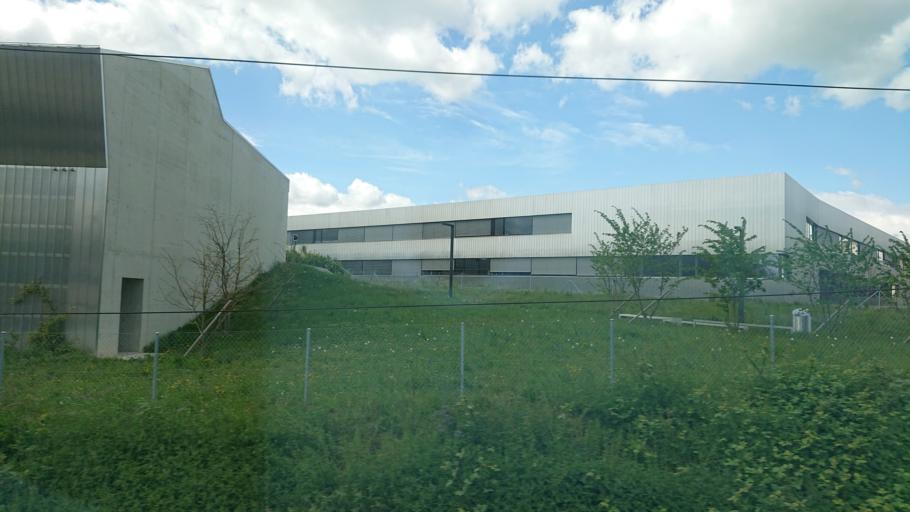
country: CH
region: Vaud
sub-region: Nyon District
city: Nyon
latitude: 46.3814
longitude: 6.2321
